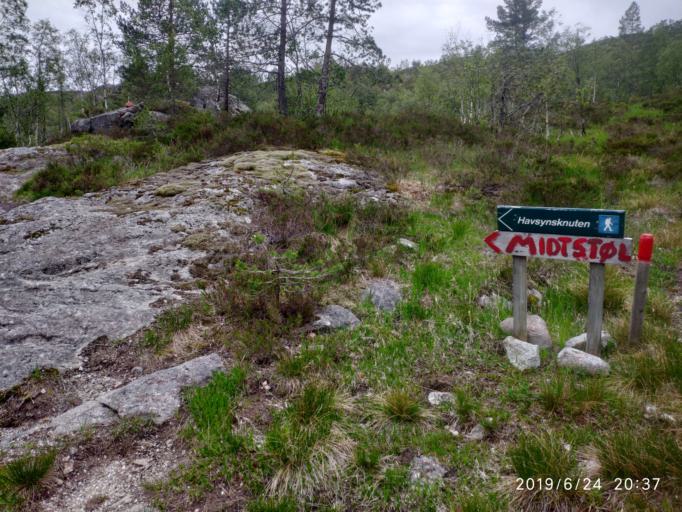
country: NO
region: Vest-Agder
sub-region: Sirdal
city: Tonstad
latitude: 58.7631
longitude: 6.7289
